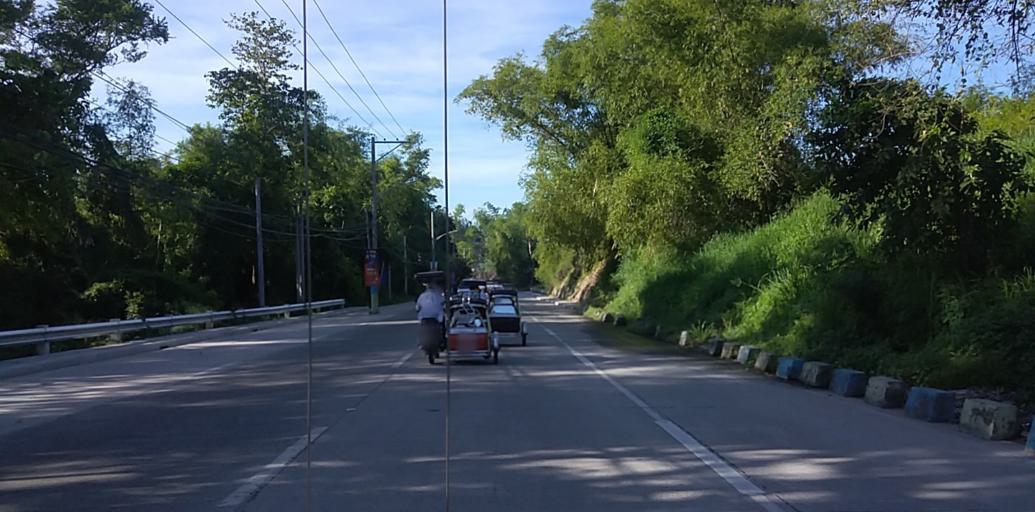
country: PH
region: Central Luzon
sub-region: Province of Pampanga
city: Porac
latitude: 15.0787
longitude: 120.5458
